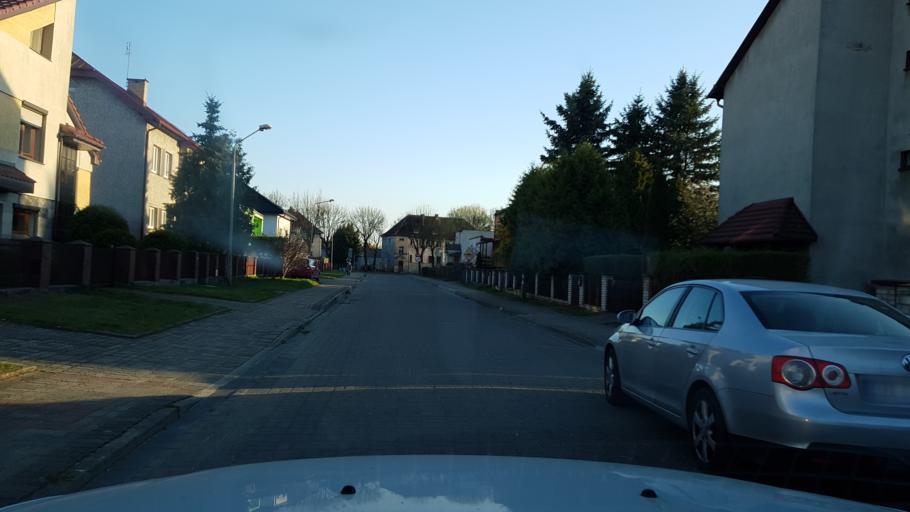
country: PL
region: West Pomeranian Voivodeship
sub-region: Powiat bialogardzki
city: Bialogard
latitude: 54.0088
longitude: 16.0038
